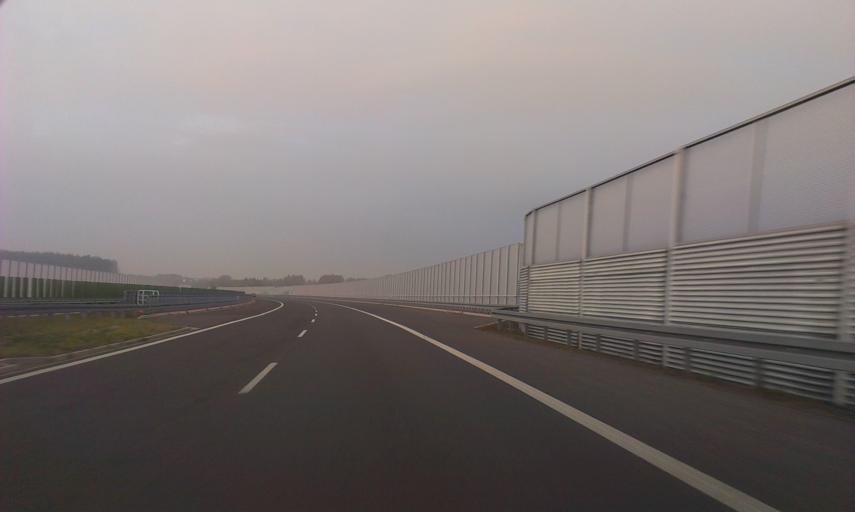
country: PL
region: Greater Poland Voivodeship
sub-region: Powiat poznanski
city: Rokietnica
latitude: 52.5155
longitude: 16.7895
